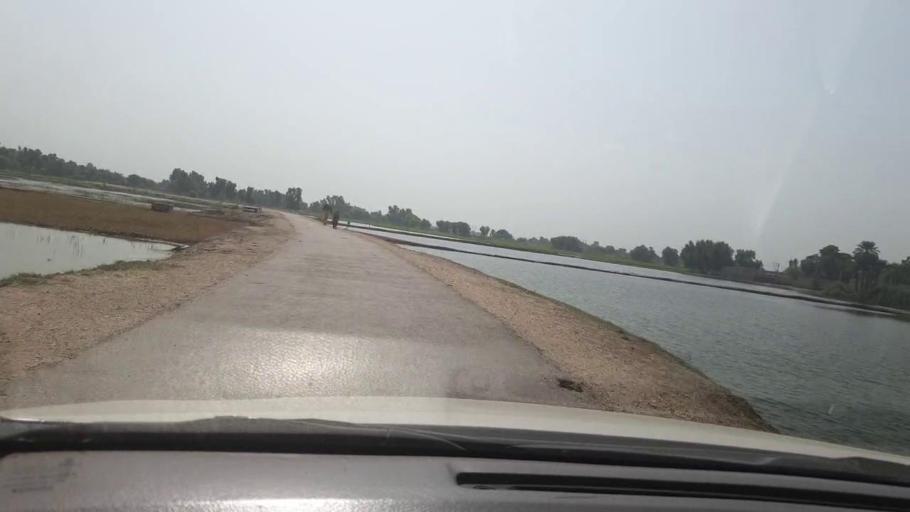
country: PK
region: Sindh
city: Rustam jo Goth
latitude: 27.9740
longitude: 68.7715
